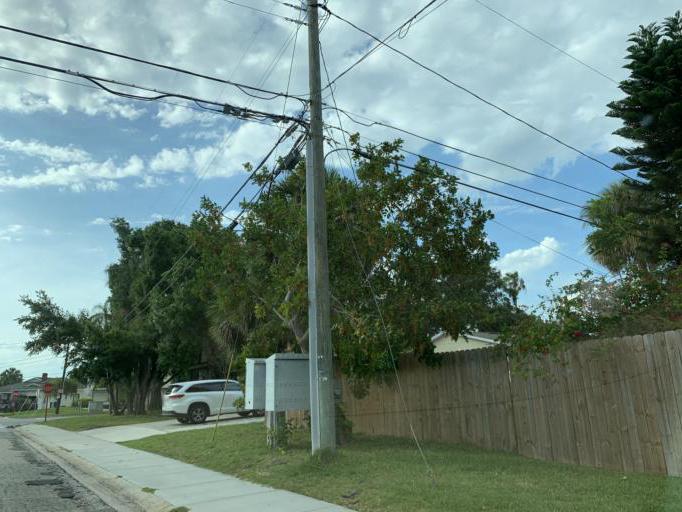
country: US
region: Florida
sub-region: Pinellas County
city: Gandy
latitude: 27.8206
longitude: -82.5999
